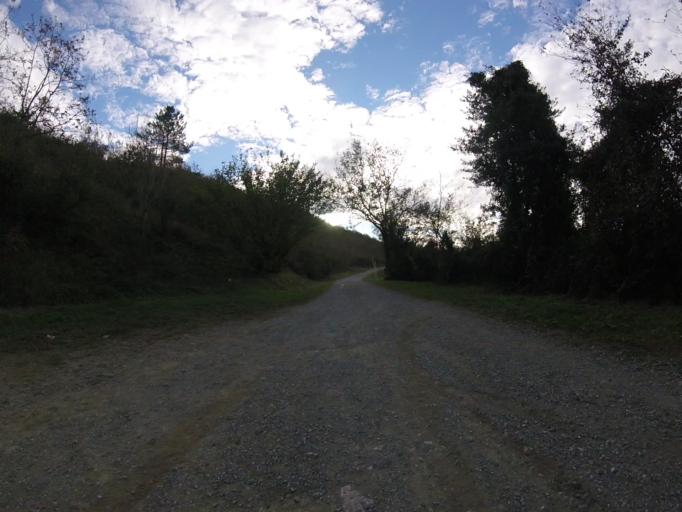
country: ES
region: Basque Country
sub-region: Provincia de Guipuzcoa
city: Errenteria
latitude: 43.2988
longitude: -1.9174
